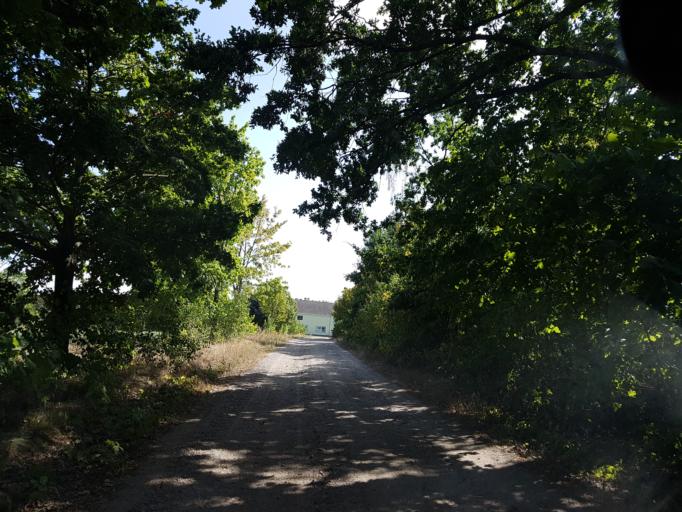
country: DE
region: Brandenburg
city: Treuenbrietzen
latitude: 52.0270
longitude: 12.8134
